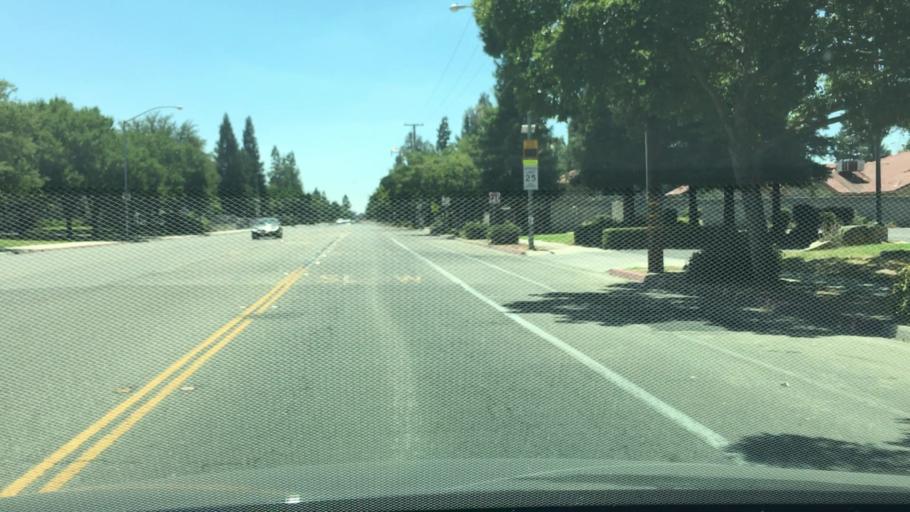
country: US
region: California
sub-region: Fresno County
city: Clovis
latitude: 36.8588
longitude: -119.7479
